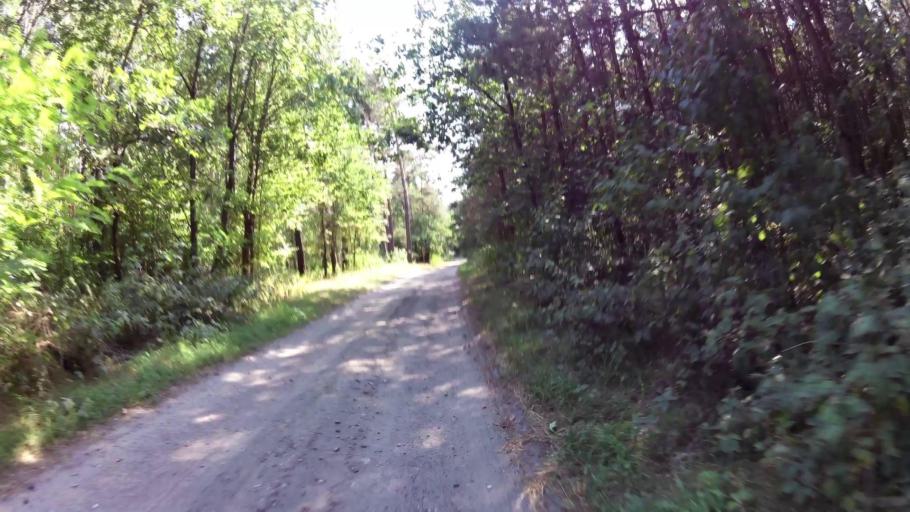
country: PL
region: West Pomeranian Voivodeship
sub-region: Powiat gryfinski
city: Moryn
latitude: 52.8709
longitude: 14.4280
